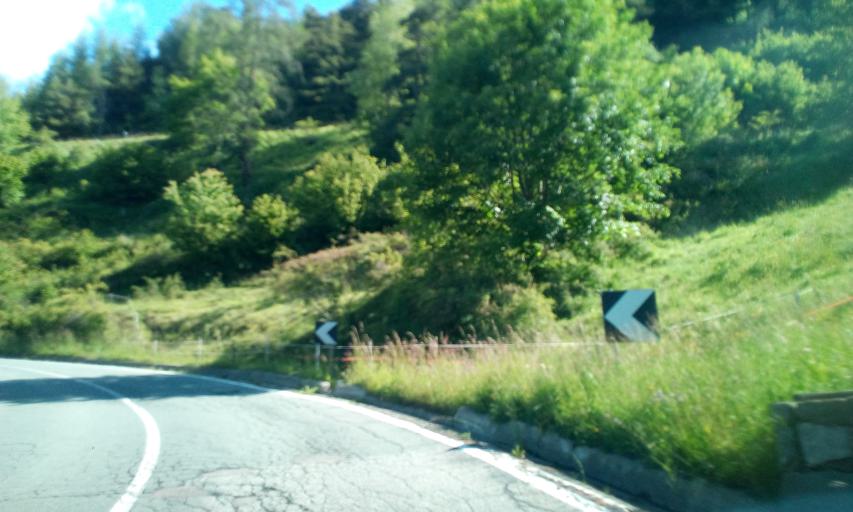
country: IT
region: Aosta Valley
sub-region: Valle d'Aosta
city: Emarese
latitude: 45.7592
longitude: 7.6877
